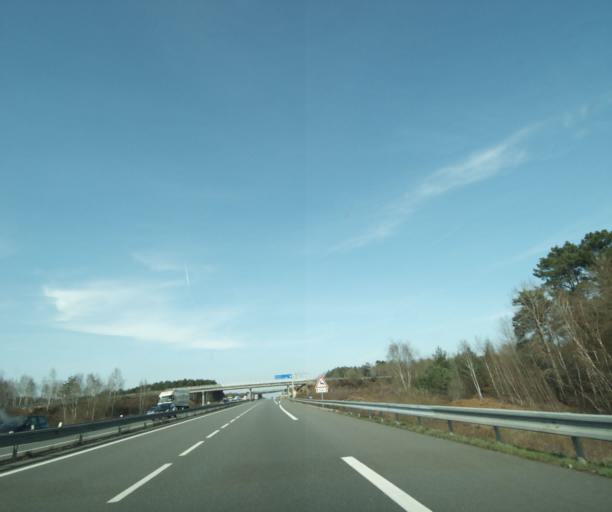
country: FR
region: Centre
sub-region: Departement du Loir-et-Cher
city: Theillay
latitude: 47.3437
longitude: 2.0484
